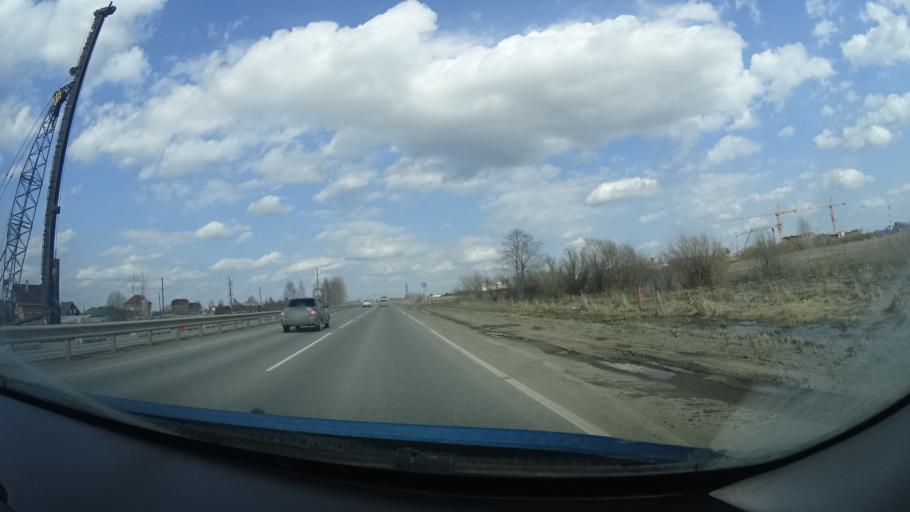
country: RU
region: Perm
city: Kultayevo
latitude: 57.9162
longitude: 56.0022
